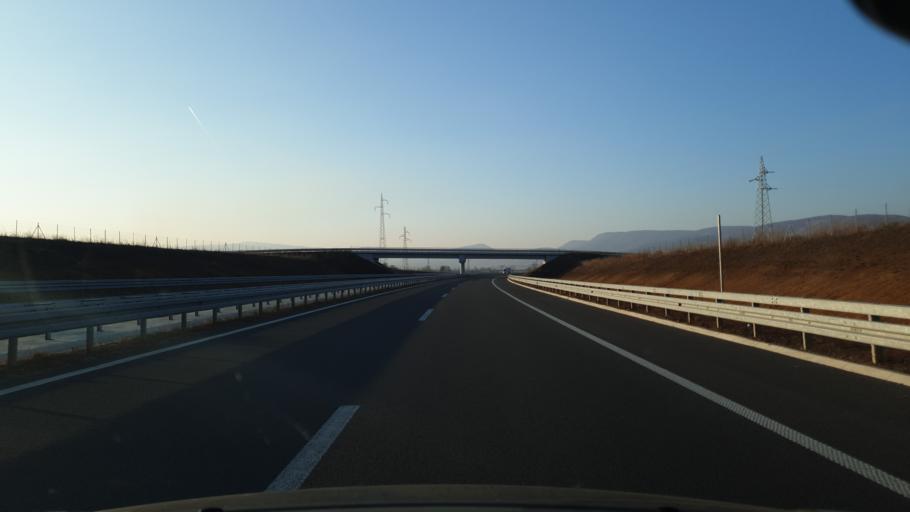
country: RS
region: Central Serbia
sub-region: Pirotski Okrug
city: Pirot
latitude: 43.1287
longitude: 22.5804
